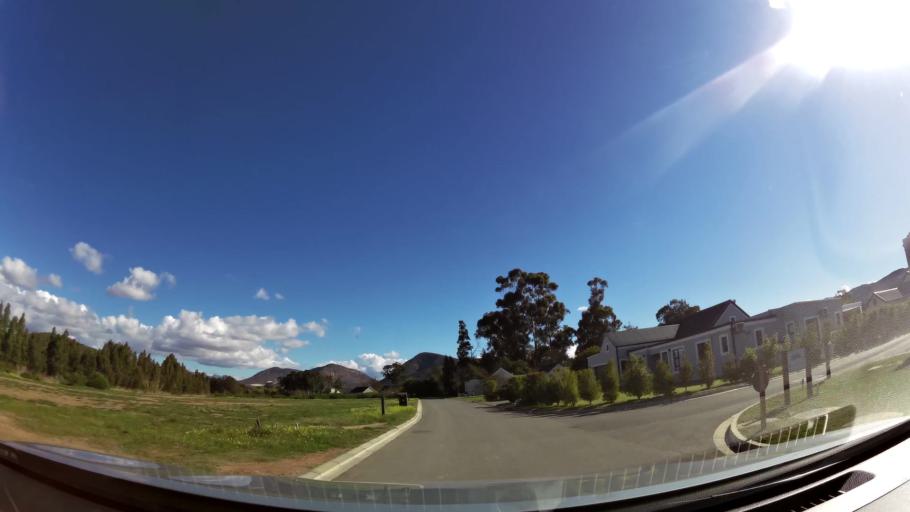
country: ZA
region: Western Cape
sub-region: Cape Winelands District Municipality
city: Ashton
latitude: -33.8124
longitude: 19.8553
